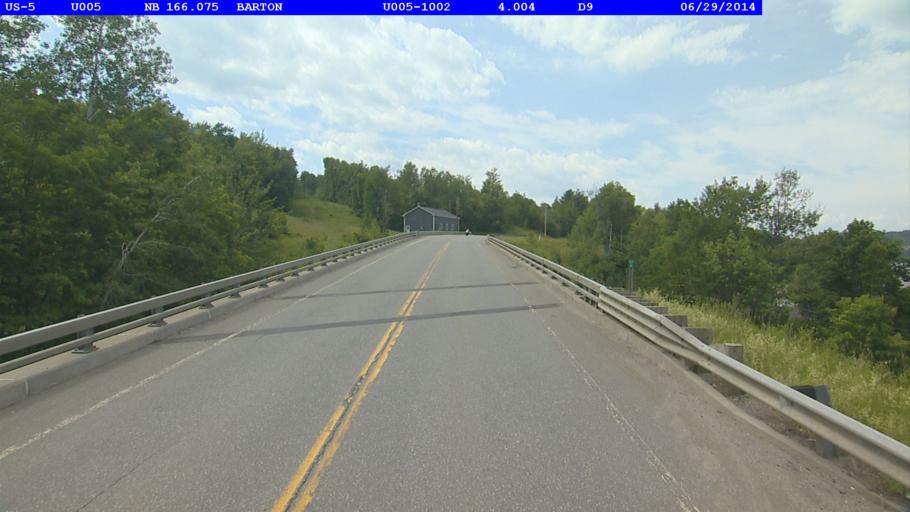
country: US
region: Vermont
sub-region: Orleans County
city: Newport
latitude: 44.7318
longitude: -72.1600
